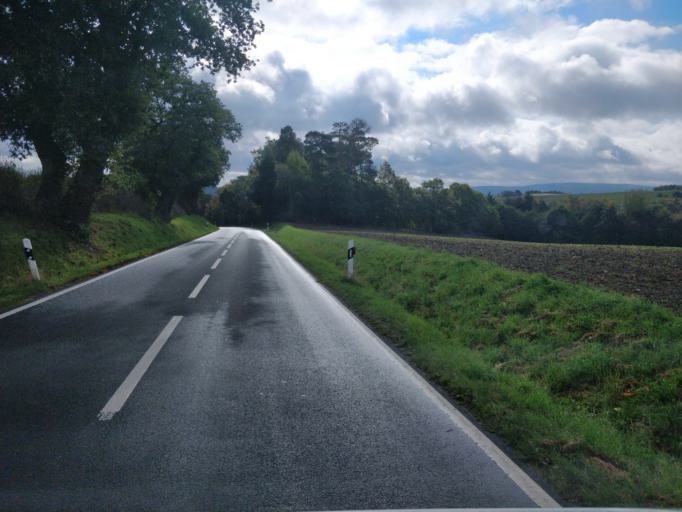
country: DE
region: Hesse
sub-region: Regierungsbezirk Darmstadt
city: Usingen
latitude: 50.3389
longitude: 8.5143
